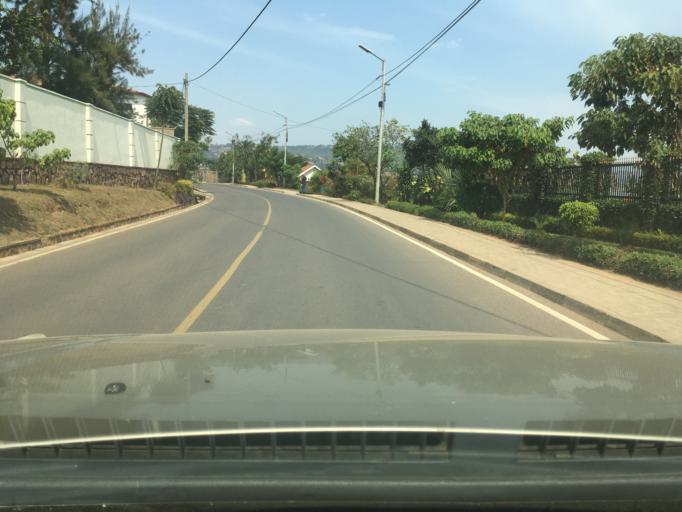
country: RW
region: Kigali
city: Kigali
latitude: -1.9634
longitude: 30.1017
